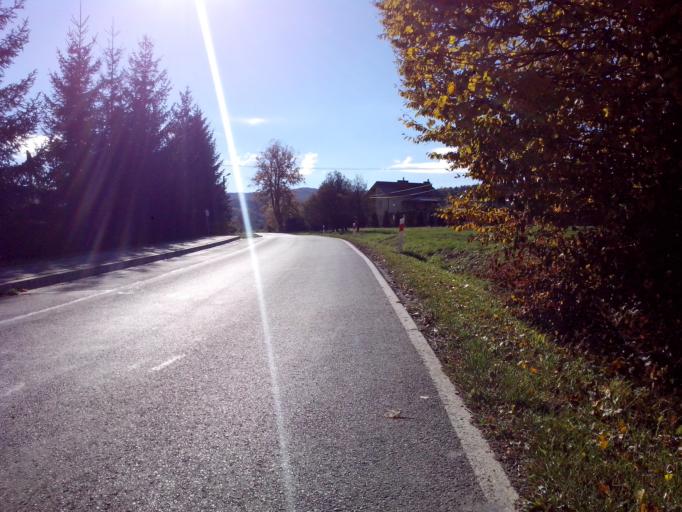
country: PL
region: Subcarpathian Voivodeship
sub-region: Powiat krosnienski
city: Korczyna
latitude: 49.7763
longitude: 21.8528
